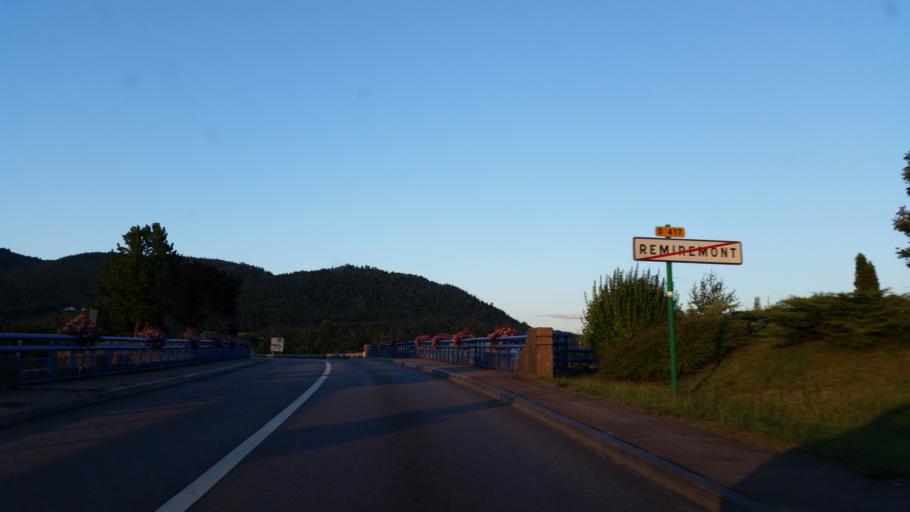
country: FR
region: Lorraine
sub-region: Departement des Vosges
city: Saint-Etienne-les-Remiremont
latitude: 48.0128
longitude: 6.6037
